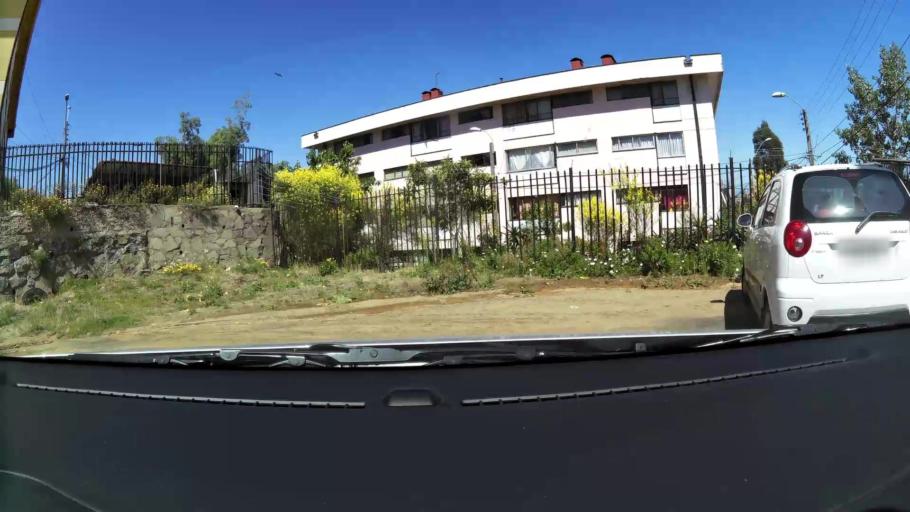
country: CL
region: Valparaiso
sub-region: Provincia de Valparaiso
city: Vina del Mar
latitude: -33.0556
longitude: -71.5818
